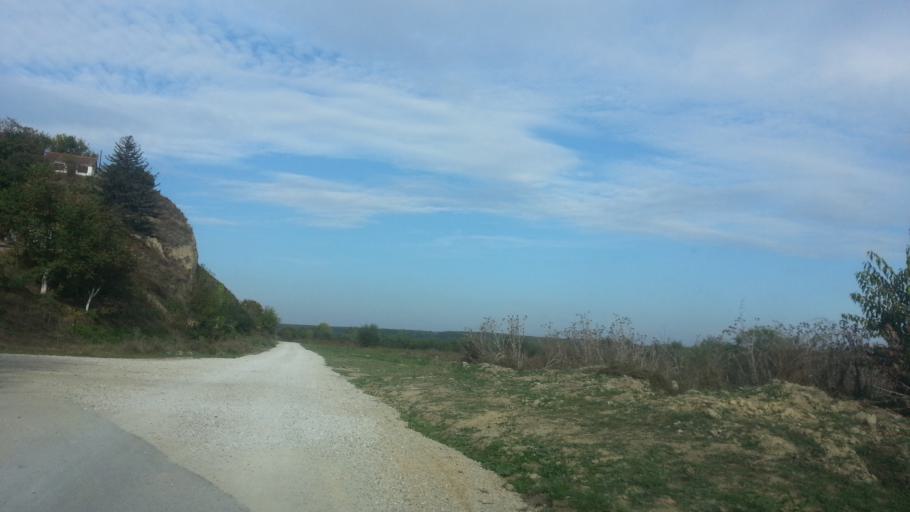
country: RS
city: Belegis
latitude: 45.0199
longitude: 20.3478
